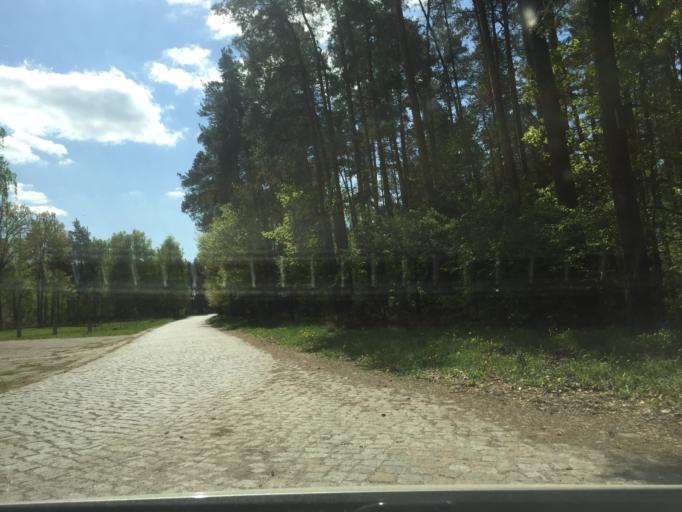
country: DE
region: Mecklenburg-Vorpommern
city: Torgelow
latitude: 53.6287
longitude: 13.9868
